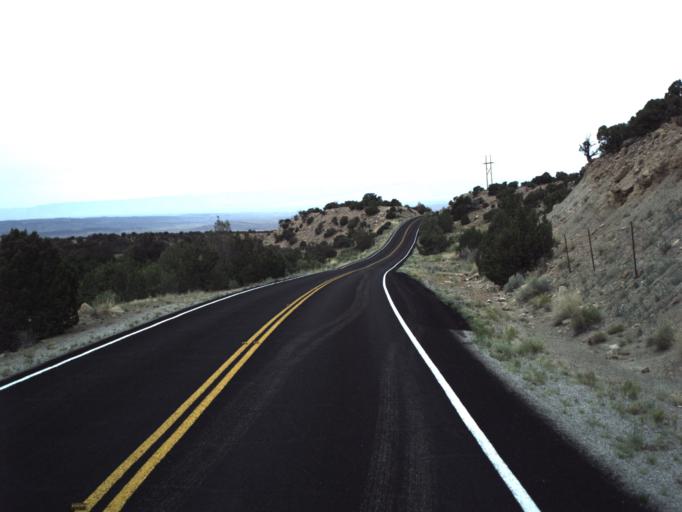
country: US
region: Utah
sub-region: Carbon County
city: East Carbon City
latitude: 39.4525
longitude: -110.3749
